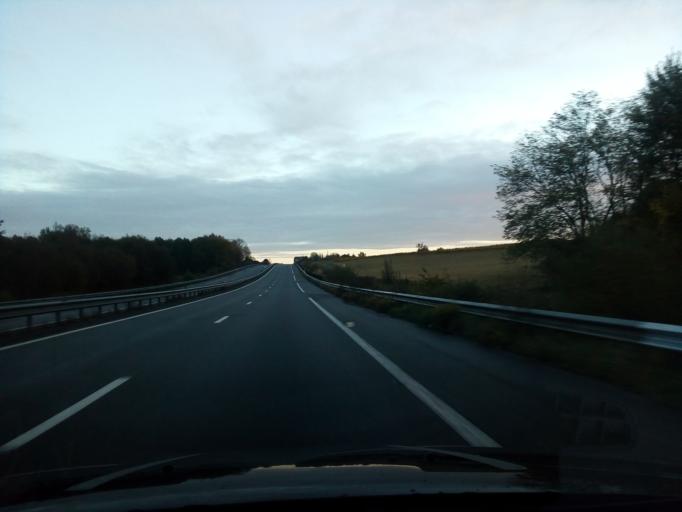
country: FR
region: Poitou-Charentes
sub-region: Departement de la Charente-Maritime
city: Montlieu-la-Garde
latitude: 45.2244
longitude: -0.2849
